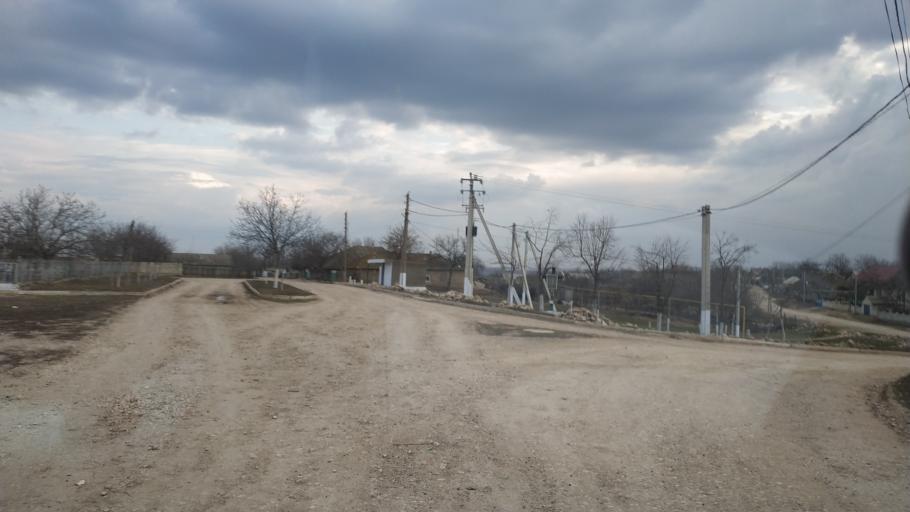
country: MD
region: Telenesti
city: Grigoriopol
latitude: 47.0250
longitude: 29.3494
